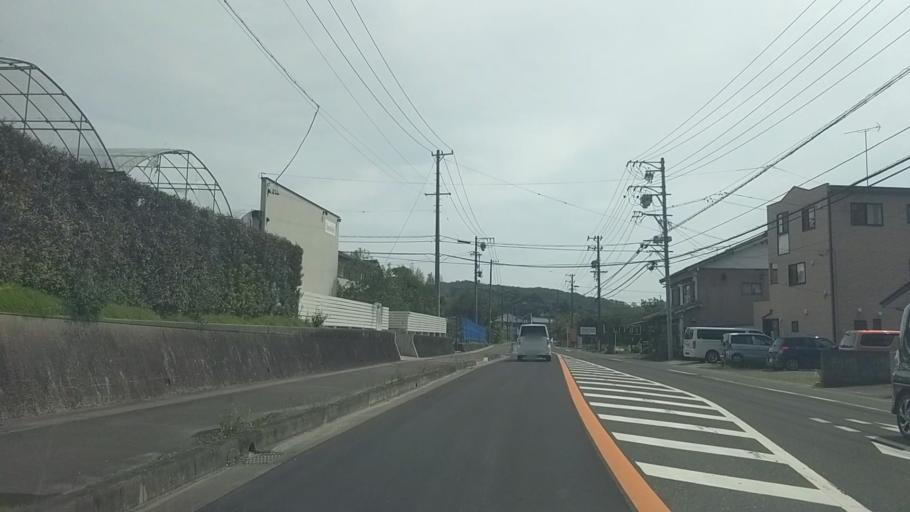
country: JP
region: Shizuoka
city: Hamamatsu
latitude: 34.7930
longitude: 137.6481
